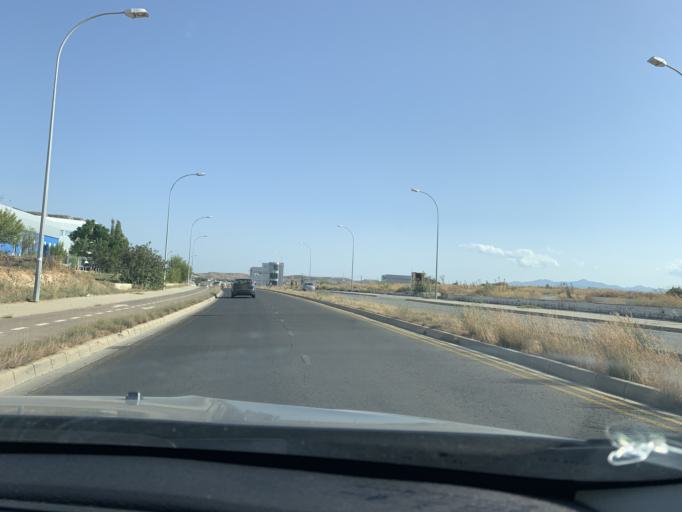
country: CY
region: Lefkosia
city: Nicosia
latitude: 35.1230
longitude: 33.3562
